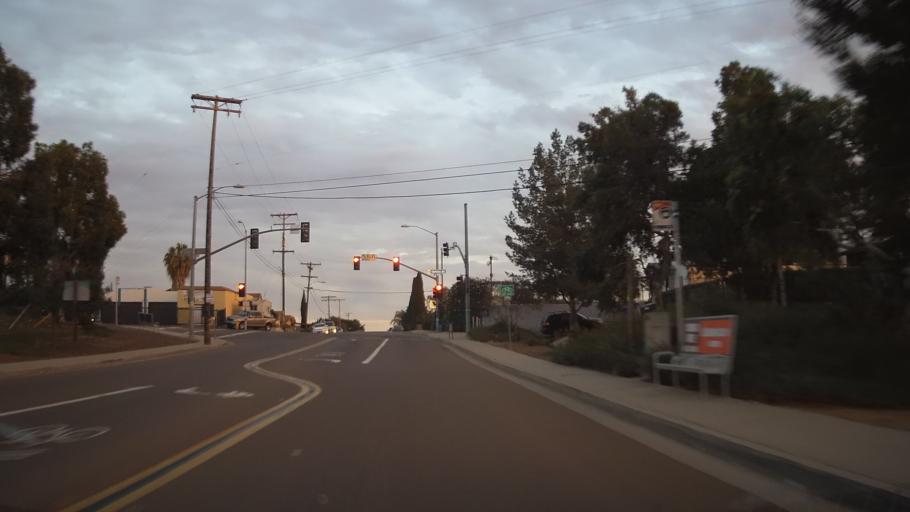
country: US
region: California
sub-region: San Diego County
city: National City
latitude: 32.7054
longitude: -117.1169
